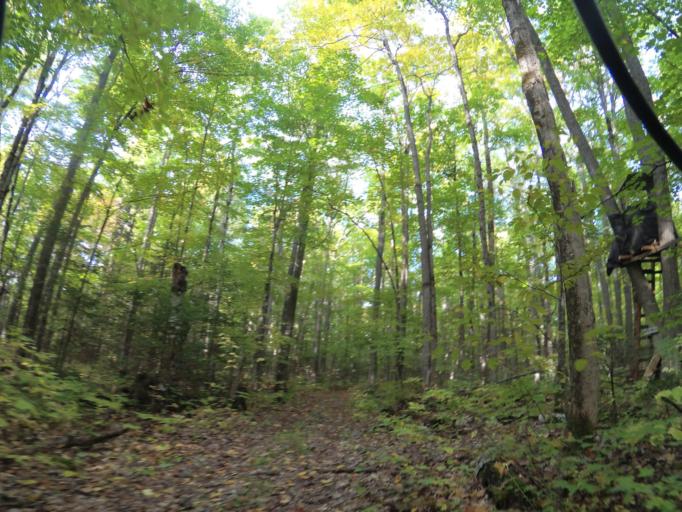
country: CA
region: Ontario
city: Pembroke
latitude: 45.3278
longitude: -77.1851
